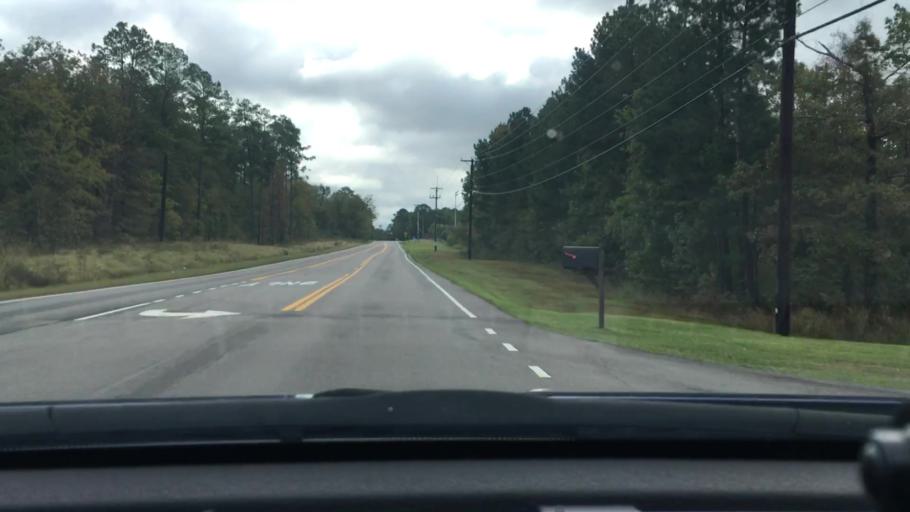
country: US
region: South Carolina
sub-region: Lexington County
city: Irmo
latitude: 34.0883
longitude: -81.1526
